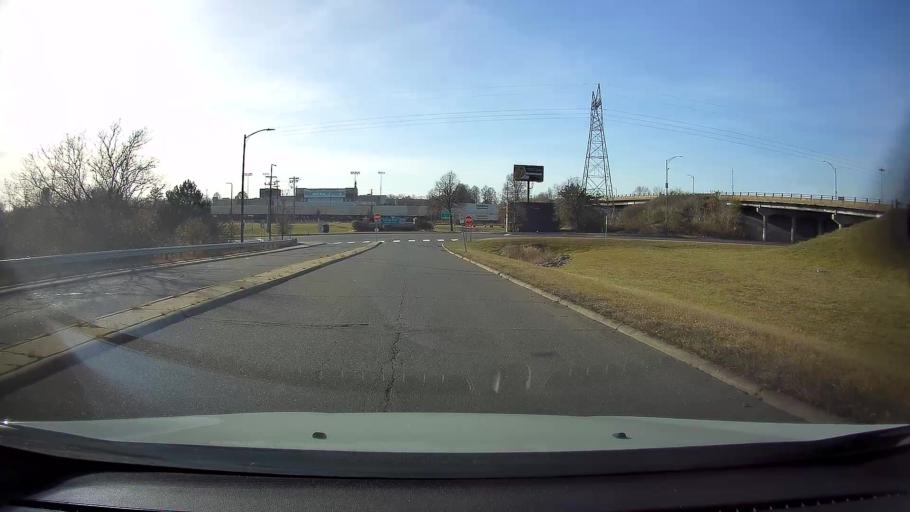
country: US
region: Minnesota
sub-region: Ramsey County
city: Falcon Heights
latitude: 44.9713
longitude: -93.1662
